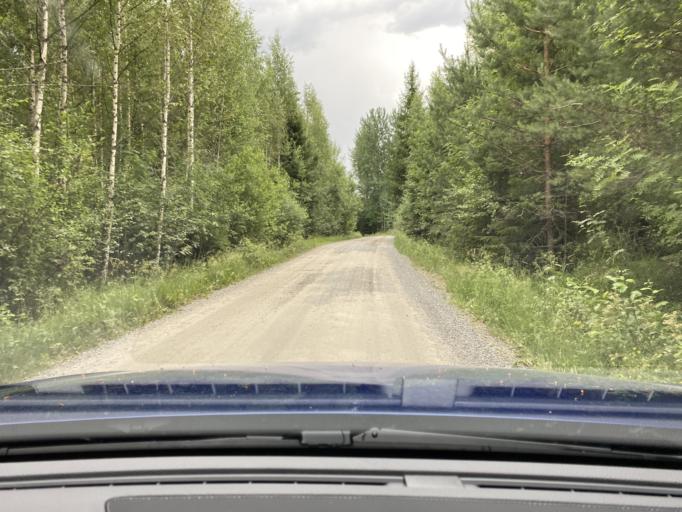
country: FI
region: Satakunta
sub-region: Rauma
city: Lappi
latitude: 61.1426
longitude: 21.9056
